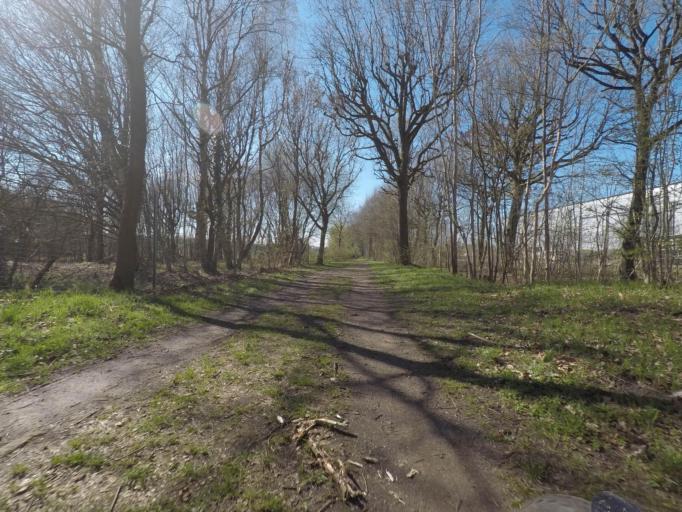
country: DE
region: Schleswig-Holstein
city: Norderstedt
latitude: 53.6599
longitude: 9.9746
